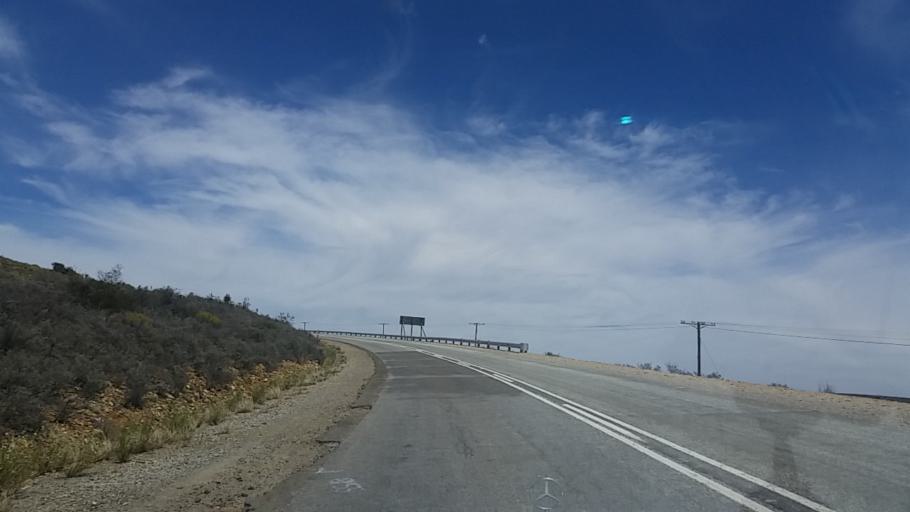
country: ZA
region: Western Cape
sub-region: Eden District Municipality
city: Knysna
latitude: -33.6289
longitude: 23.1288
